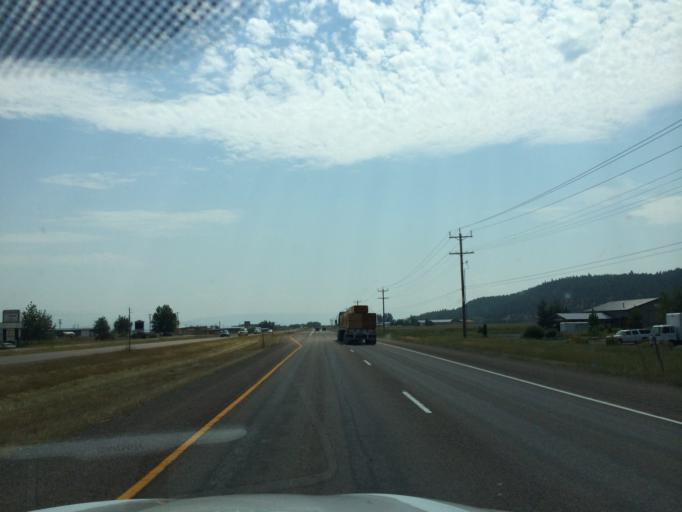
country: US
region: Montana
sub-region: Flathead County
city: Kalispell
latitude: 48.1368
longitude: -114.2752
